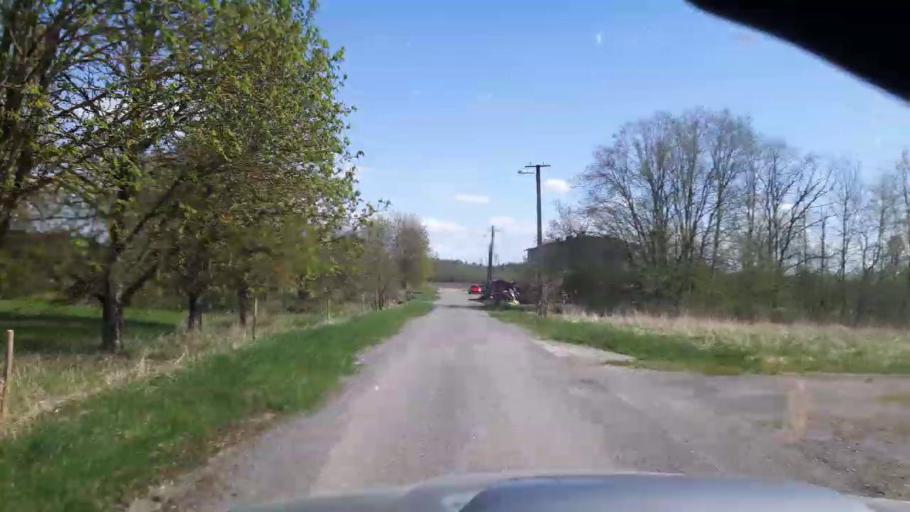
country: EE
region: Paernumaa
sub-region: Tootsi vald
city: Tootsi
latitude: 58.5373
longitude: 24.8920
